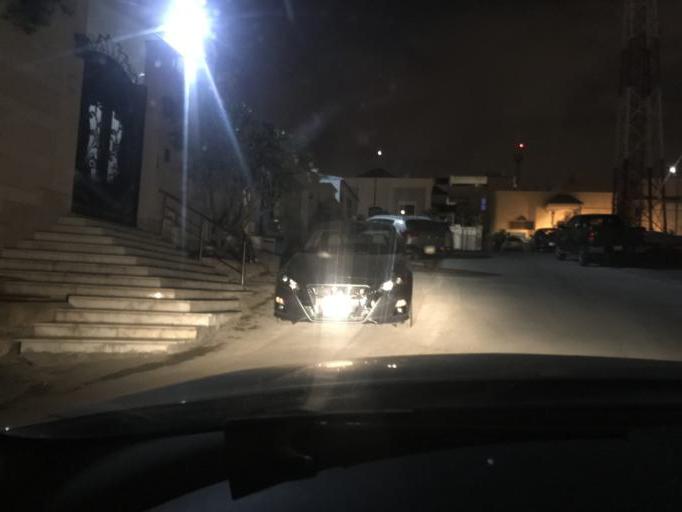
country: SA
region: Ar Riyad
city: Riyadh
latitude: 24.7748
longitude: 46.6913
